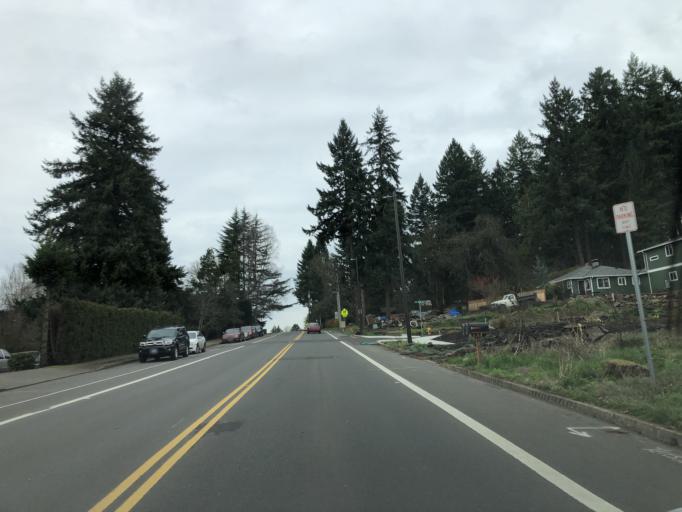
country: US
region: Oregon
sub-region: Washington County
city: Tigard
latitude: 45.4164
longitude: -122.7763
